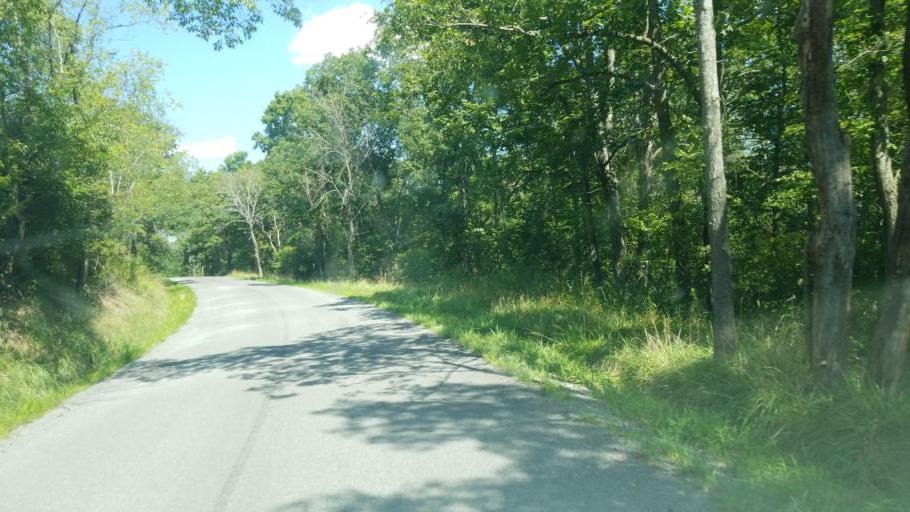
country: US
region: Pennsylvania
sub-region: Clarion County
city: Knox
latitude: 41.0959
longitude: -79.5006
